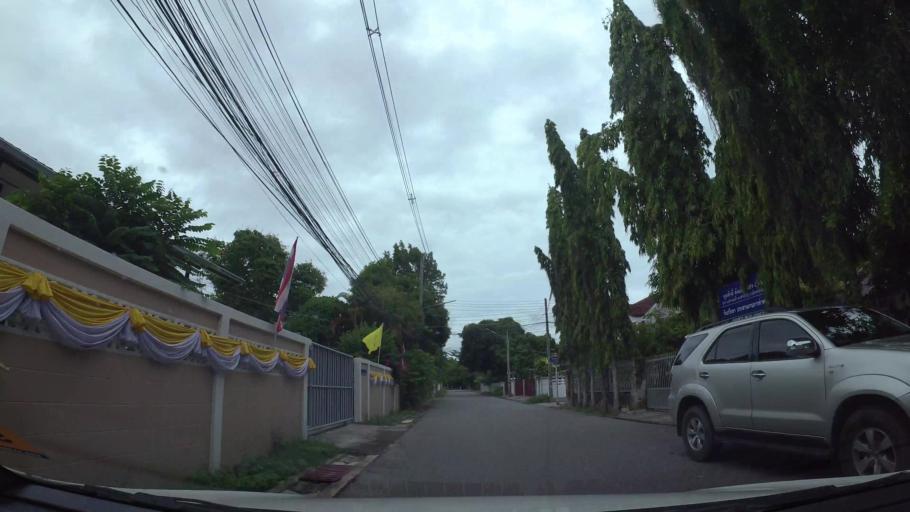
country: TH
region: Rayong
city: Rayong
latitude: 12.6732
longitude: 101.2759
